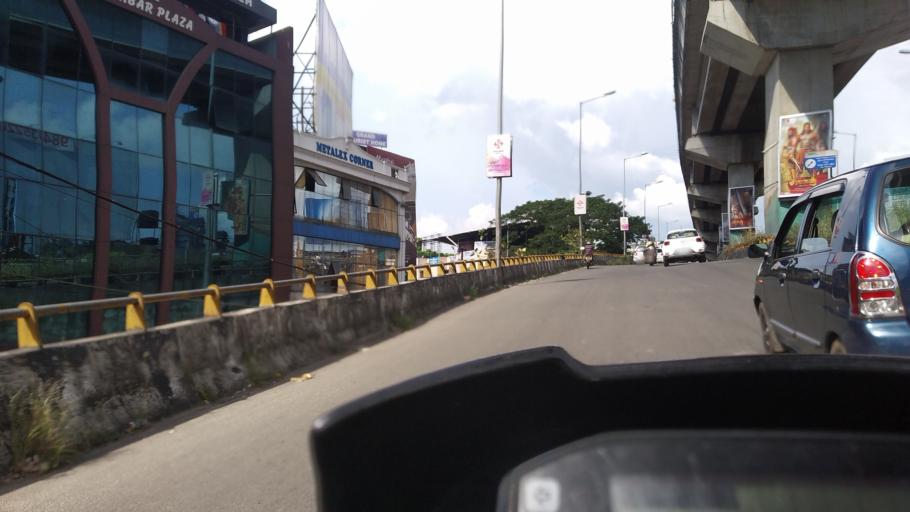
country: IN
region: Kerala
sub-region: Ernakulam
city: Cochin
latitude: 9.9891
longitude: 76.2864
